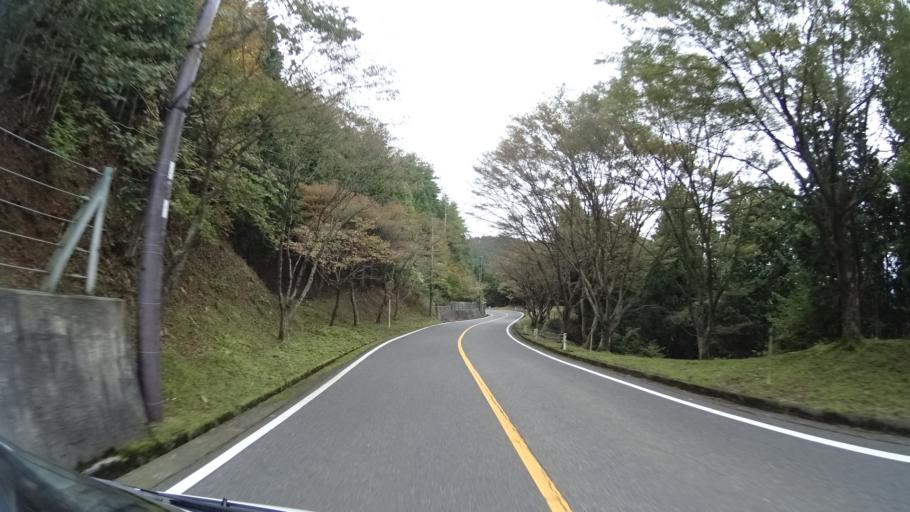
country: JP
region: Shiga Prefecture
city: Otsu-shi
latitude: 35.0882
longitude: 135.8415
